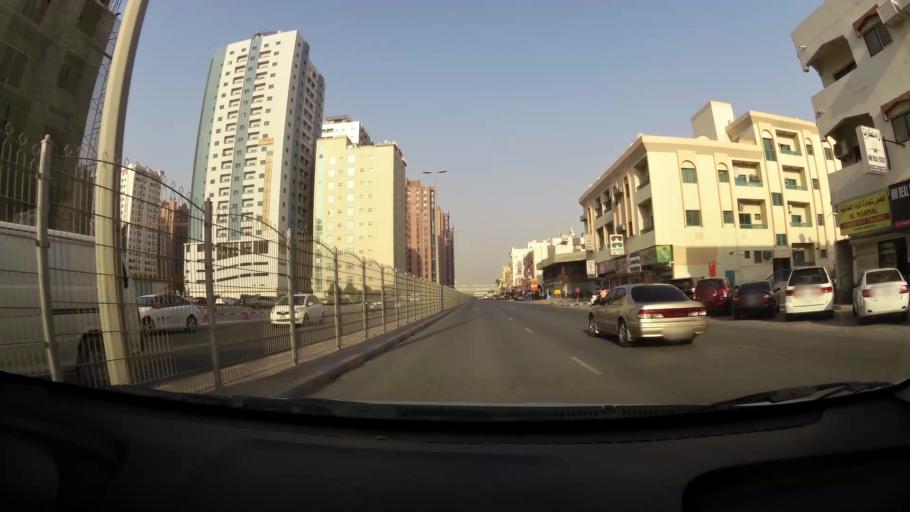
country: AE
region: Ajman
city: Ajman
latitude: 25.3862
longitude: 55.4566
